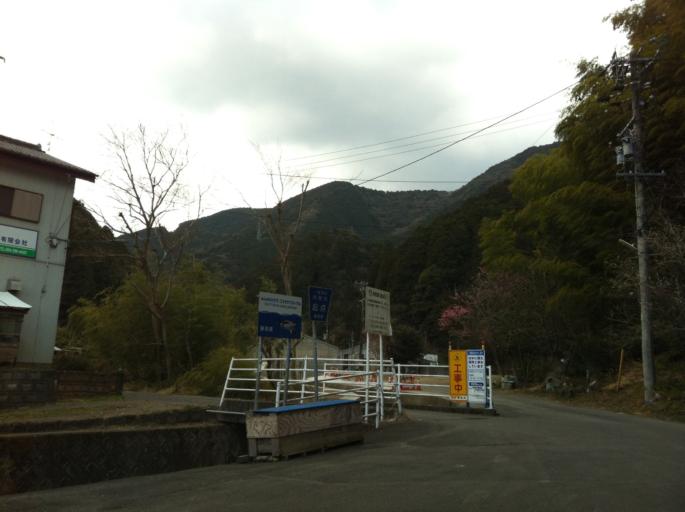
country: JP
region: Shizuoka
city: Shizuoka-shi
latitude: 35.0321
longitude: 138.3330
